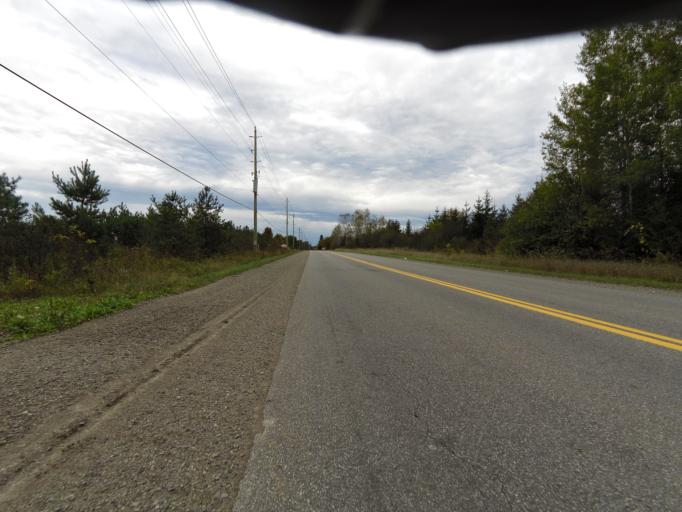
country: CA
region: Ontario
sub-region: Lanark County
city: Smiths Falls
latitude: 44.9566
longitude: -75.8232
